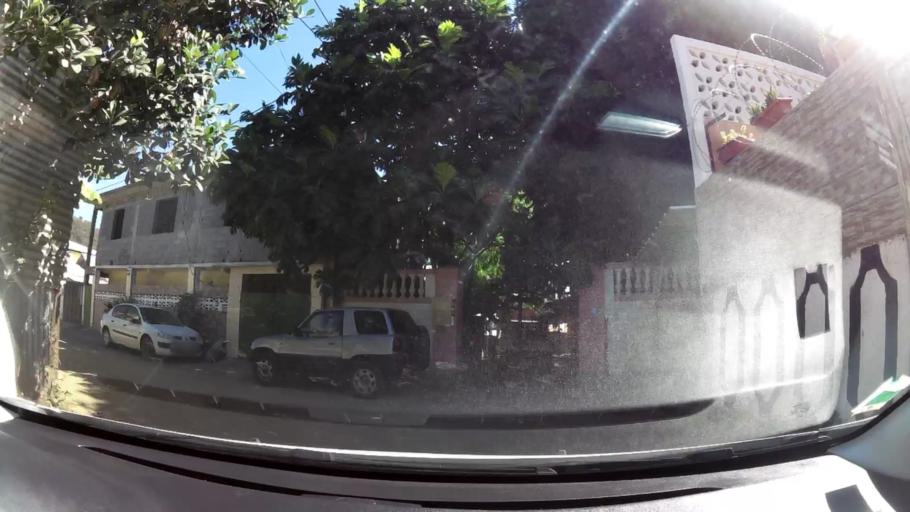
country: YT
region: Pamandzi
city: Pamandzi
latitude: -12.7858
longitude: 45.2786
